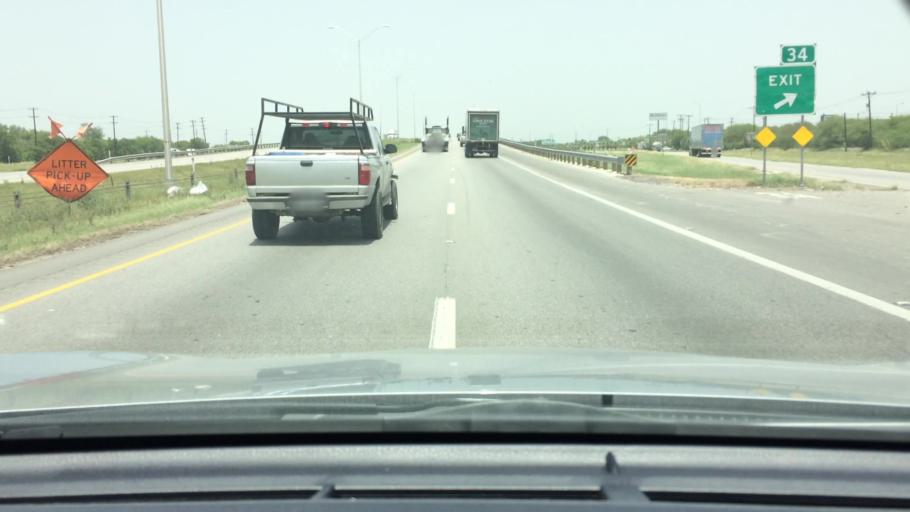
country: US
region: Texas
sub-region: Bexar County
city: Kirby
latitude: 29.4200
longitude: -98.3892
